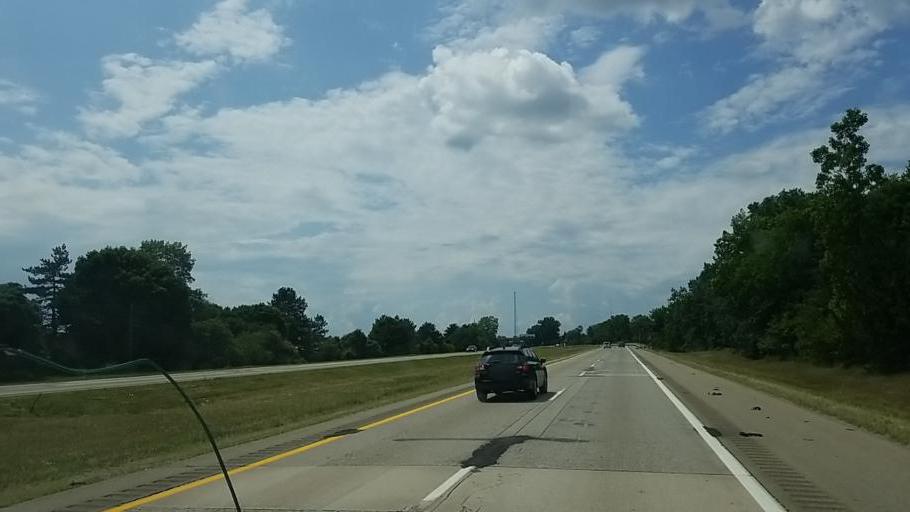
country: US
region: Michigan
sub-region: Kent County
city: East Grand Rapids
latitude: 42.9770
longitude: -85.6195
